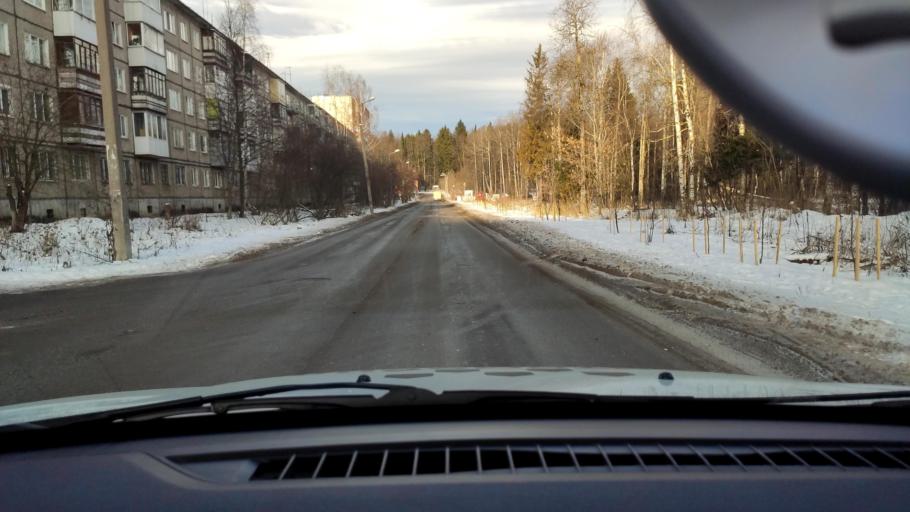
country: RU
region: Perm
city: Perm
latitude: 58.0864
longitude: 56.4134
